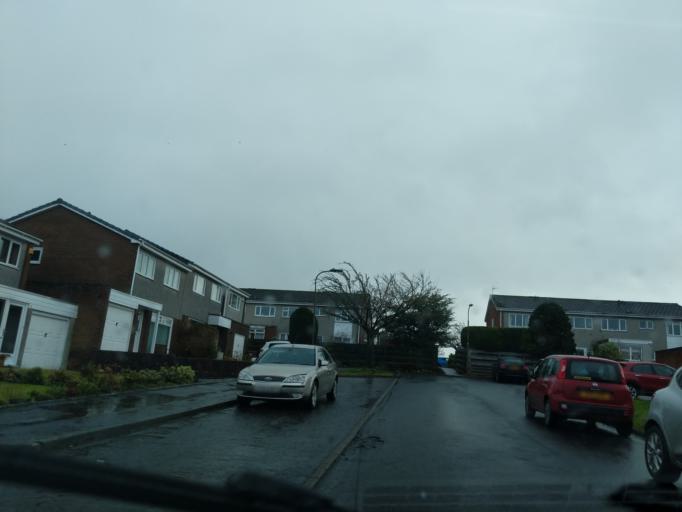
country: GB
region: Scotland
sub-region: Edinburgh
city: Balerno
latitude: 55.8750
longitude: -3.3444
